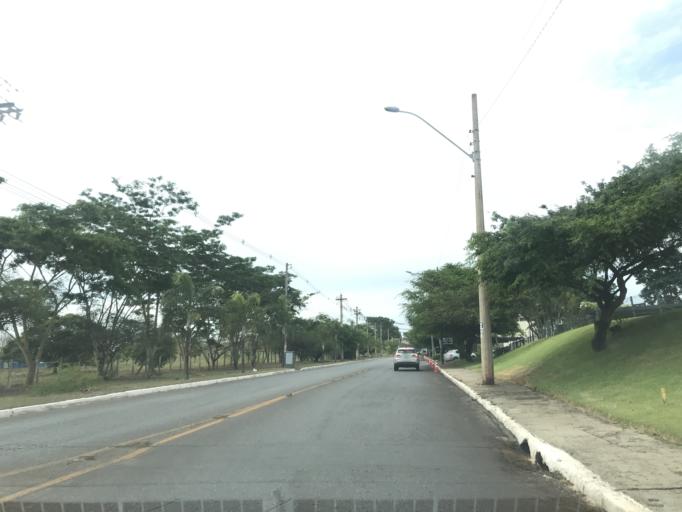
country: BR
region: Federal District
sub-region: Brasilia
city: Brasilia
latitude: -15.7218
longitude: -47.8870
